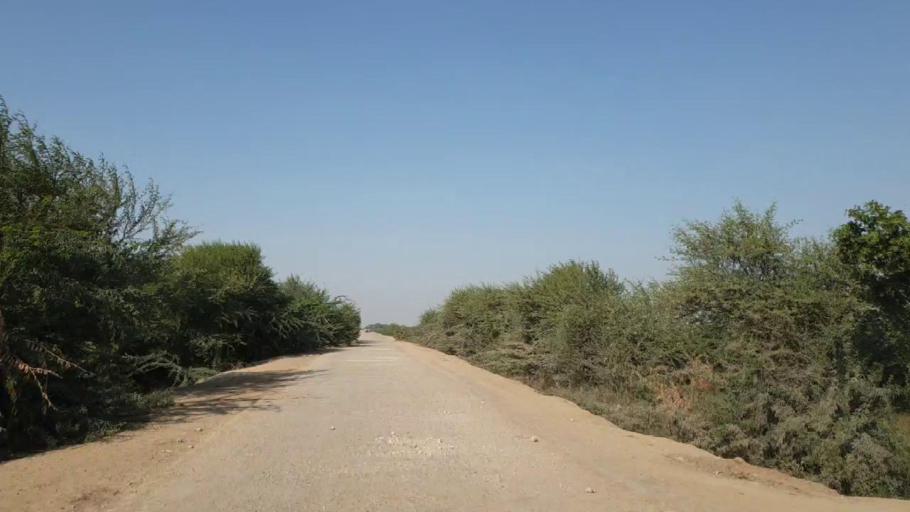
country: PK
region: Sindh
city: Digri
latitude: 24.9859
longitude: 69.1097
